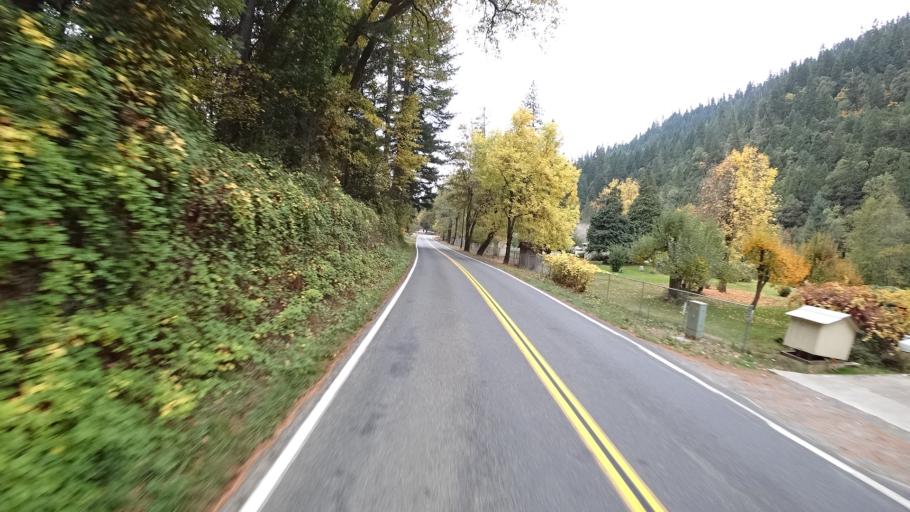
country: US
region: California
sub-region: Siskiyou County
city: Happy Camp
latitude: 41.8310
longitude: -123.3837
